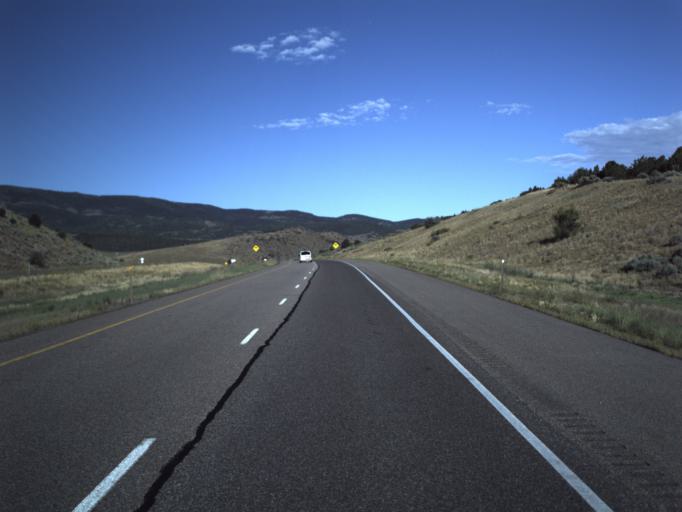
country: US
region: Utah
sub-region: Sevier County
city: Monroe
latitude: 38.5533
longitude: -112.4109
